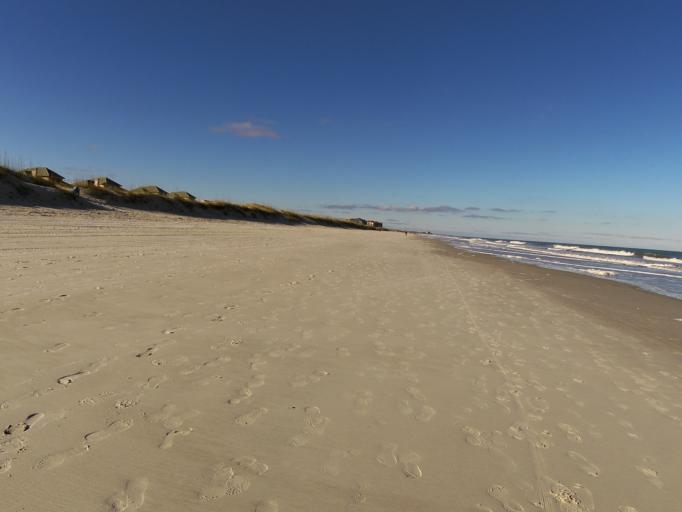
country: US
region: Florida
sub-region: Nassau County
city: Fernandina Beach
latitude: 30.5789
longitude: -81.4431
